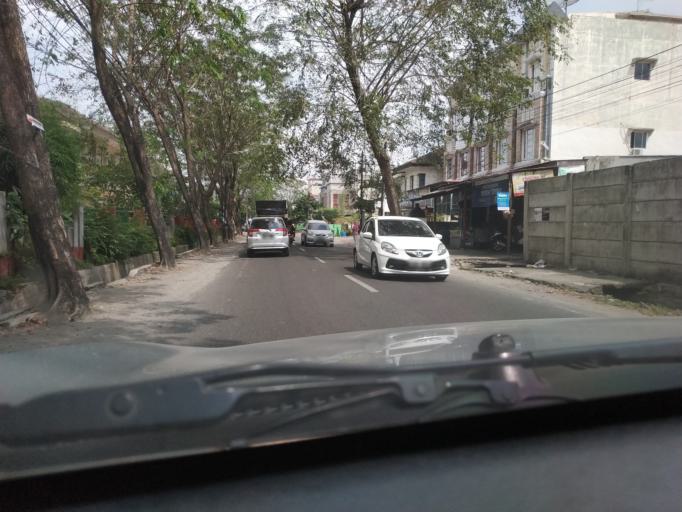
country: ID
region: North Sumatra
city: Sunggal
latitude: 3.5845
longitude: 98.6348
